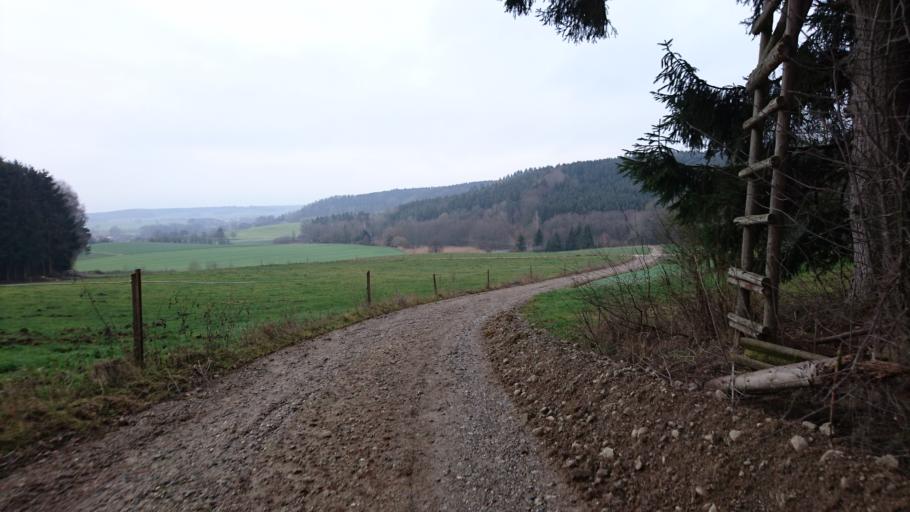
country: DE
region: Bavaria
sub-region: Swabia
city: Altenmunster
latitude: 48.4422
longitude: 10.6093
